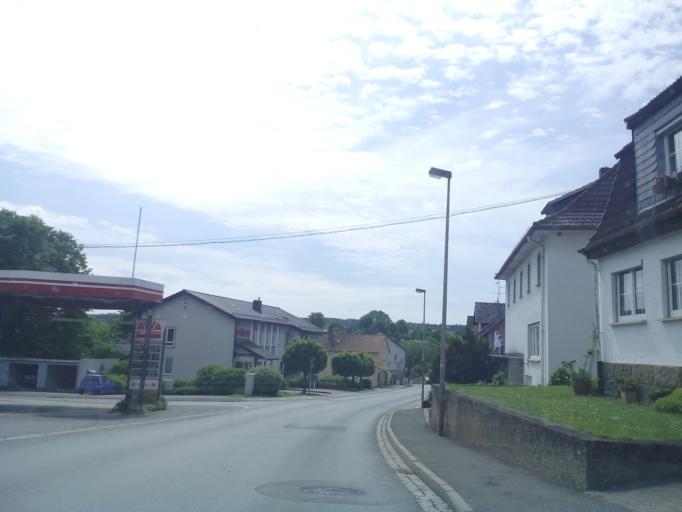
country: DE
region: Bavaria
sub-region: Upper Franconia
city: Weitramsdorf
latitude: 50.2570
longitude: 10.8840
